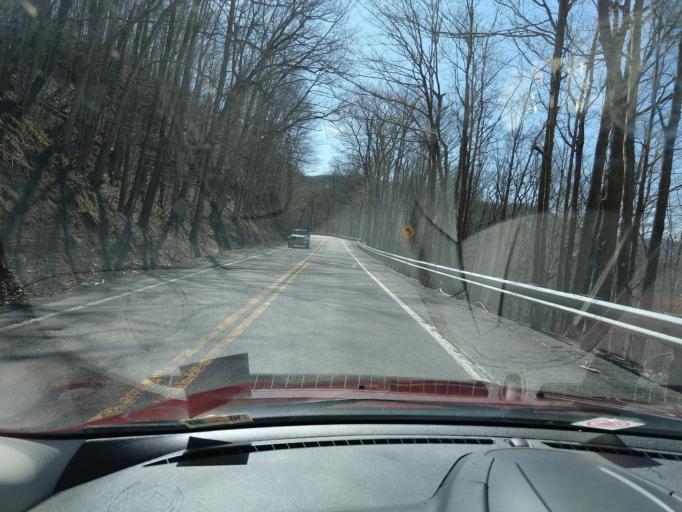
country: US
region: West Virginia
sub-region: Summers County
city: Hinton
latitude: 37.7488
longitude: -80.9129
